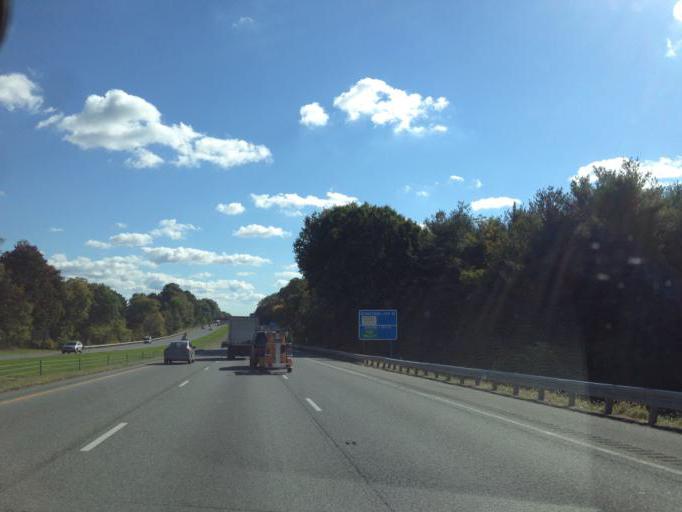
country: US
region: Maryland
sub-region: Carroll County
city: Sykesville
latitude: 39.3073
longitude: -76.9394
